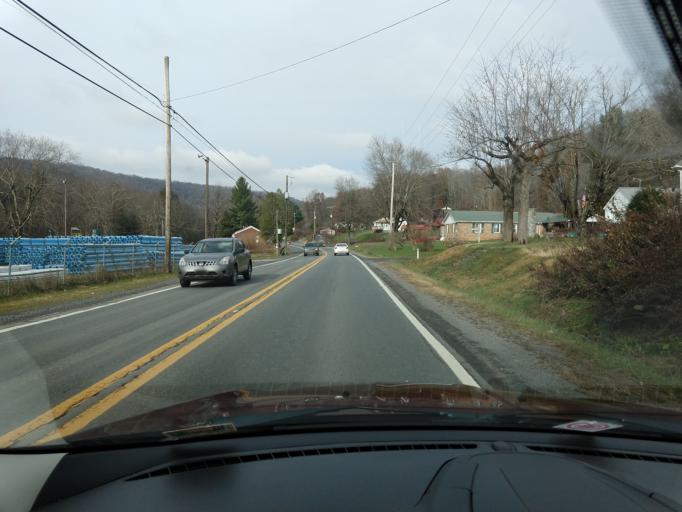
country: US
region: West Virginia
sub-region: Greenbrier County
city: Rainelle
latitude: 37.9847
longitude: -80.7212
